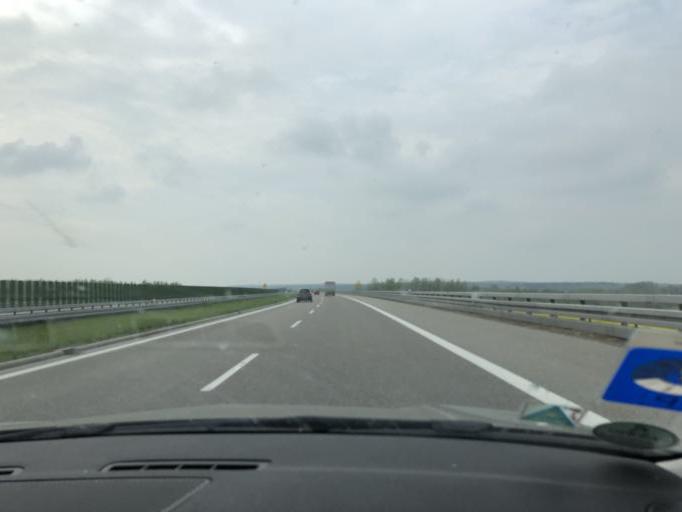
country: PL
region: Subcarpathian Voivodeship
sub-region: Powiat ropczycko-sedziszowski
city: Ostrow
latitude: 50.1078
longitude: 21.5985
